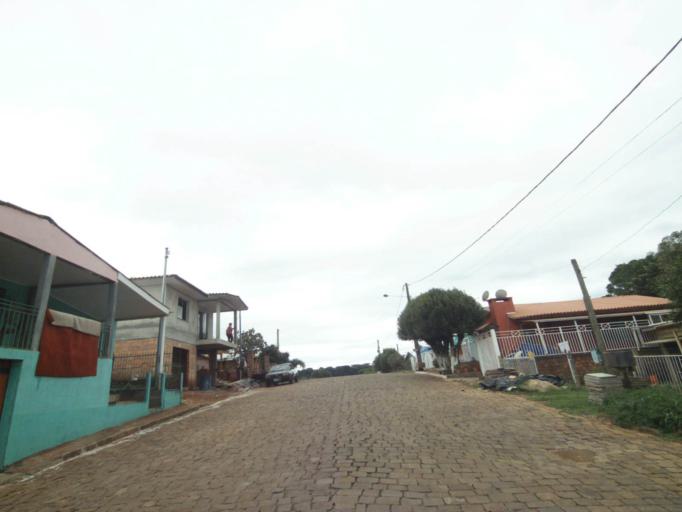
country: BR
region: Rio Grande do Sul
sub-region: Lagoa Vermelha
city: Lagoa Vermelha
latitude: -28.2124
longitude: -51.5049
